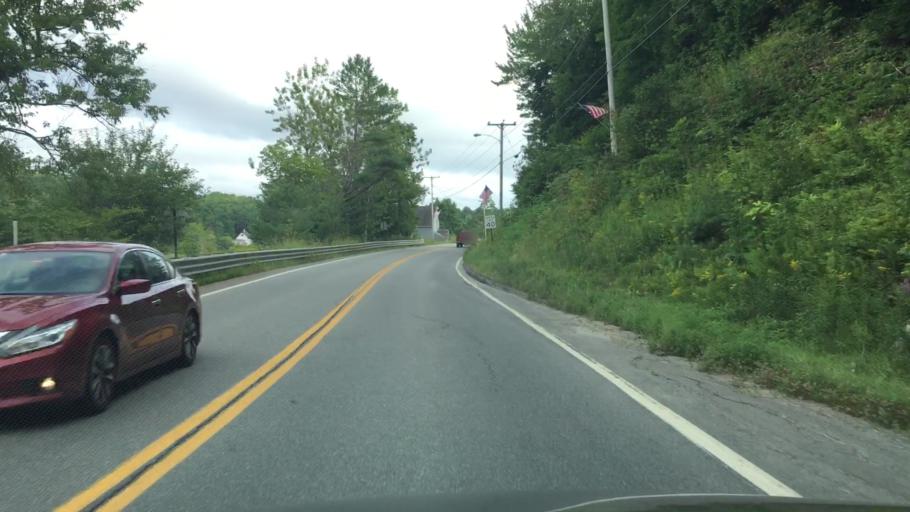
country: US
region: Maine
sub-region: Waldo County
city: Frankfort
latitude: 44.6061
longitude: -68.8729
